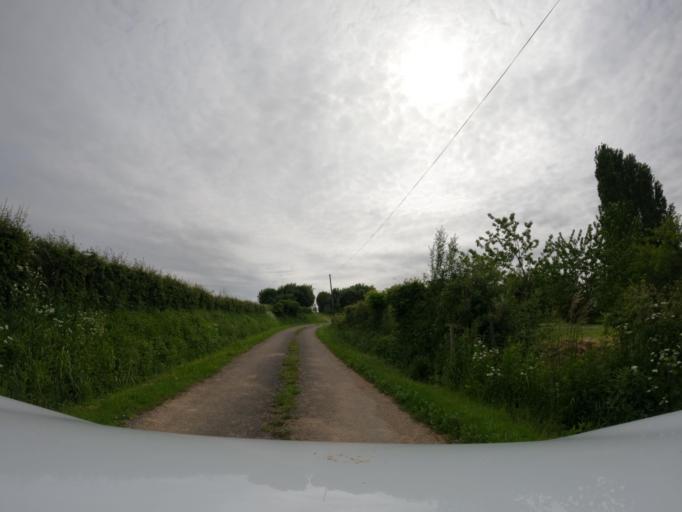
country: FR
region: Pays de la Loire
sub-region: Departement de la Vendee
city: Saint-Hilaire-des-Loges
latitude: 46.4970
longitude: -0.6711
